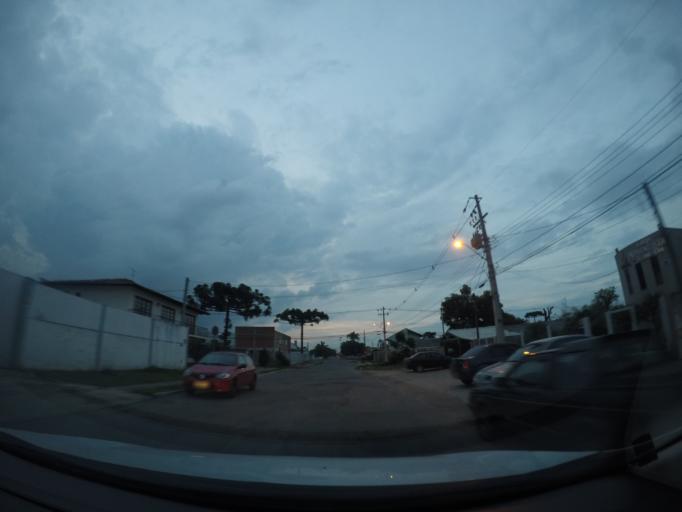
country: BR
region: Parana
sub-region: Sao Jose Dos Pinhais
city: Sao Jose dos Pinhais
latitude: -25.5007
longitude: -49.2297
